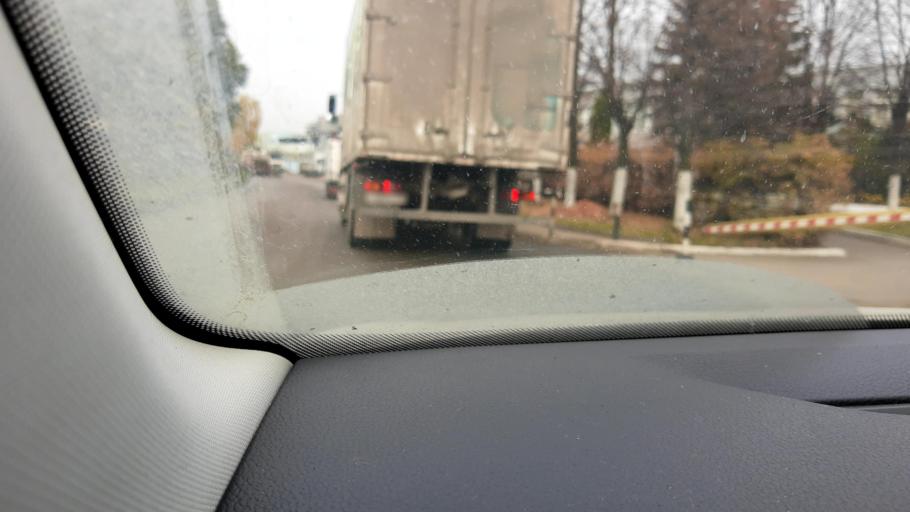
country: RU
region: Moskovskaya
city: Biryulevo Zapadnoye
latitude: 55.5762
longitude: 37.6225
